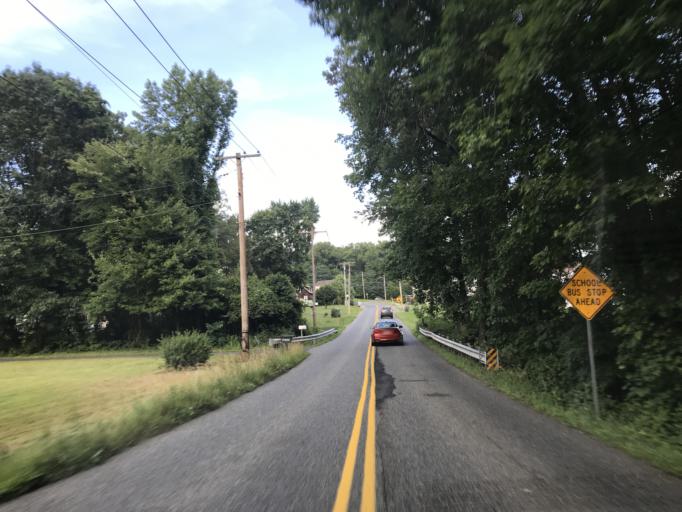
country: US
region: Maryland
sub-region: Harford County
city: Aberdeen
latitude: 39.5156
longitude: -76.1909
